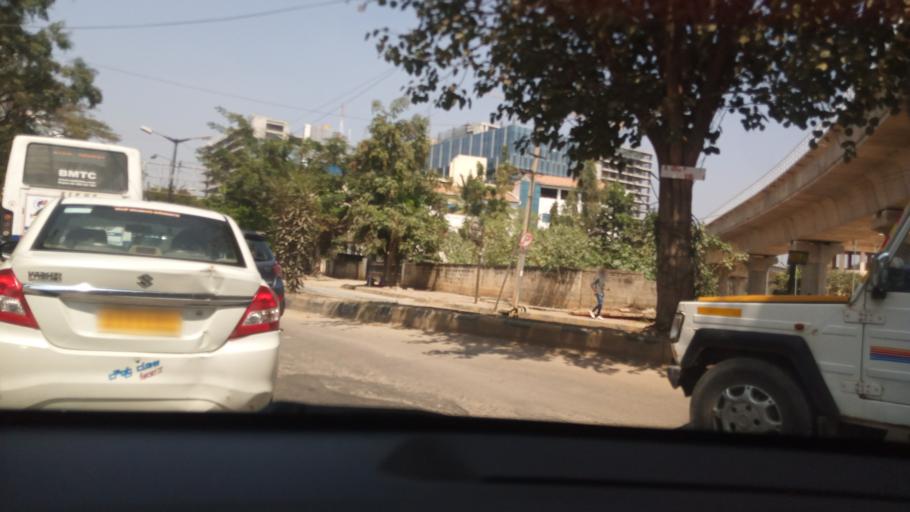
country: IN
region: Karnataka
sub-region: Bangalore Rural
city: Hoskote
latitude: 12.9866
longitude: 77.7317
